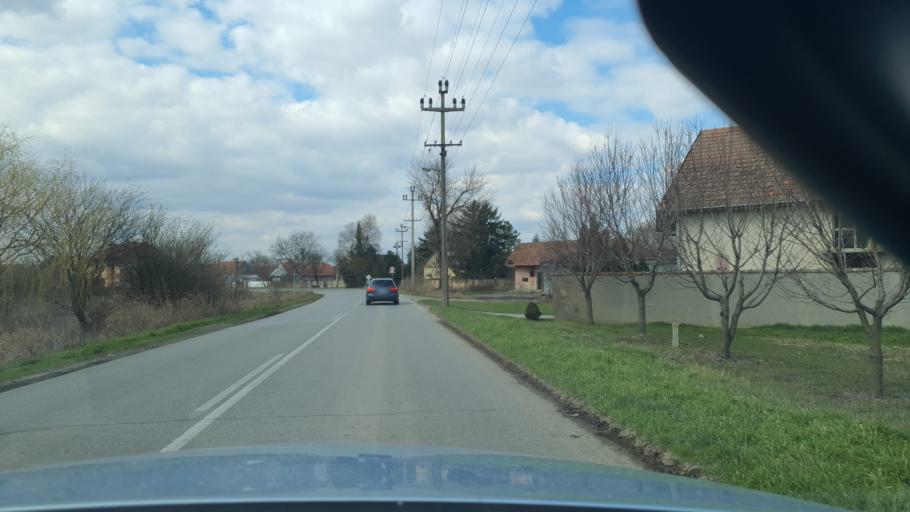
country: RS
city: Maglic
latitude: 45.3927
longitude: 19.4732
